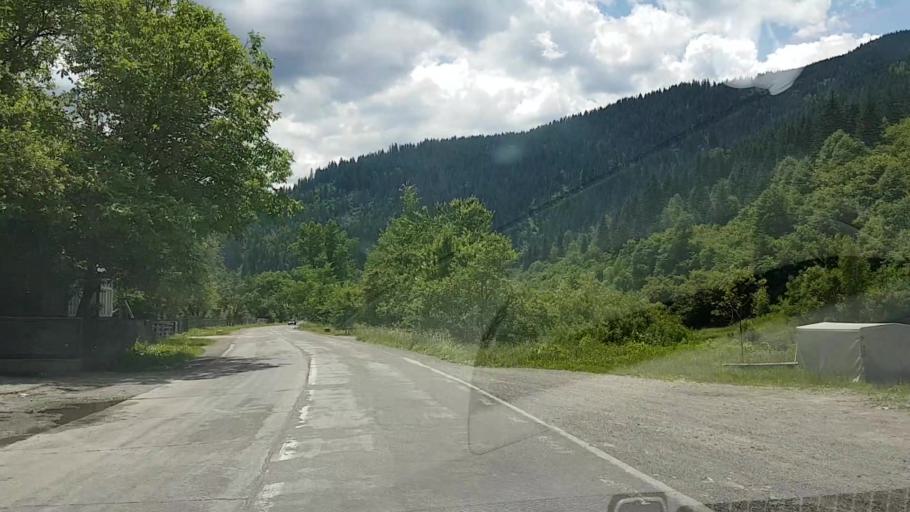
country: RO
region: Suceava
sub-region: Comuna Brosteni
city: Brosteni
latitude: 47.2474
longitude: 25.6917
